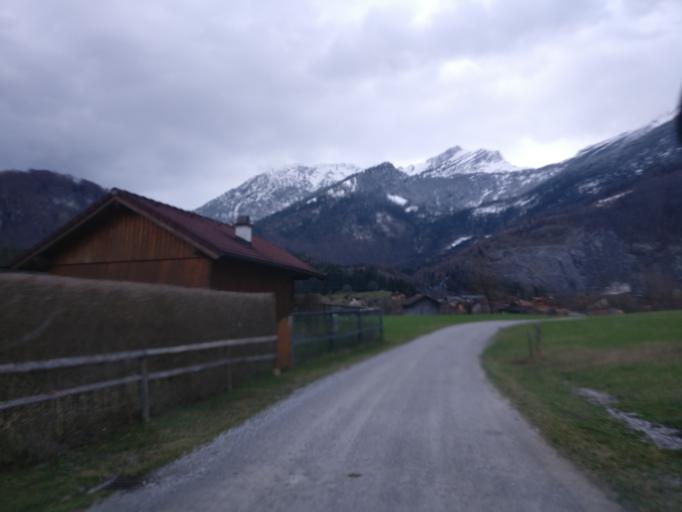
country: AT
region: Salzburg
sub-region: Politischer Bezirk Hallein
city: Golling an der Salzach
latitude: 47.5857
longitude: 13.1788
